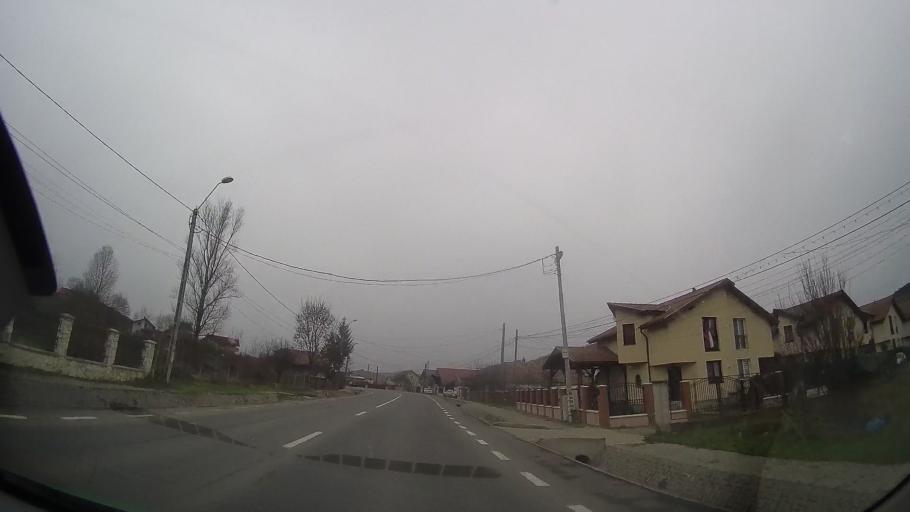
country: RO
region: Mures
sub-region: Comuna Ceausu de Campie
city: Ceausu de Campie
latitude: 46.6066
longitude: 24.5297
